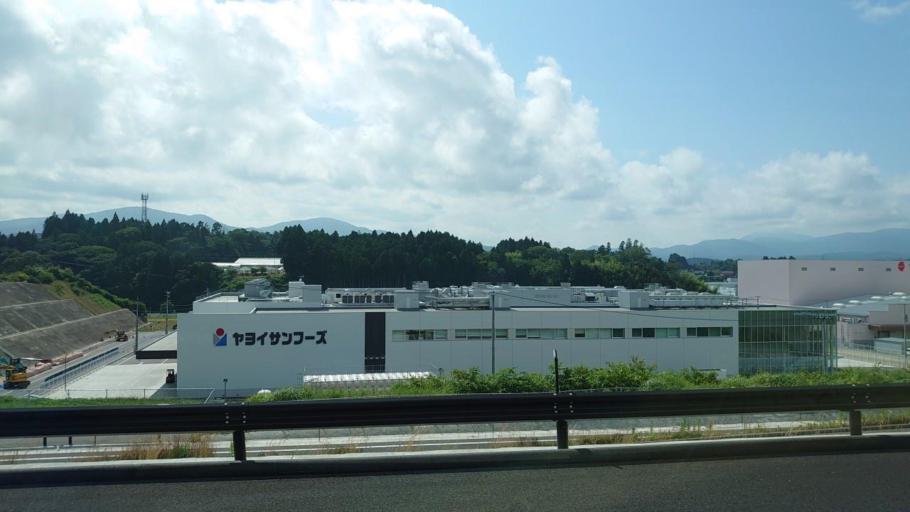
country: JP
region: Iwate
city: Ofunato
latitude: 38.8827
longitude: 141.5861
